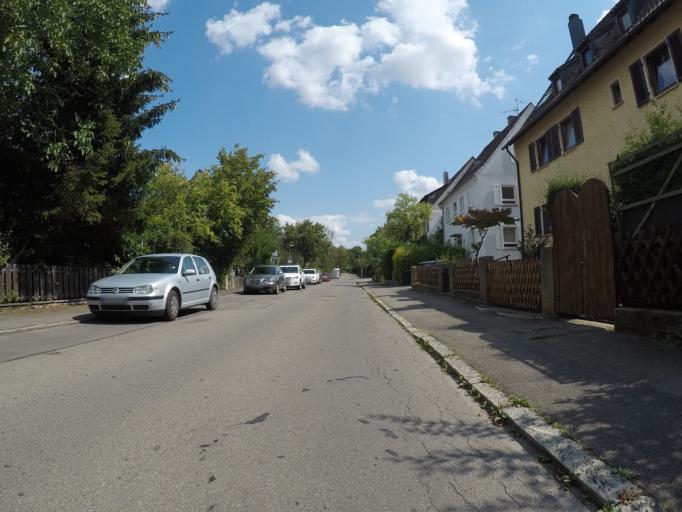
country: DE
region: Baden-Wuerttemberg
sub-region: Tuebingen Region
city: Reutlingen
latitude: 48.4906
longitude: 9.1992
